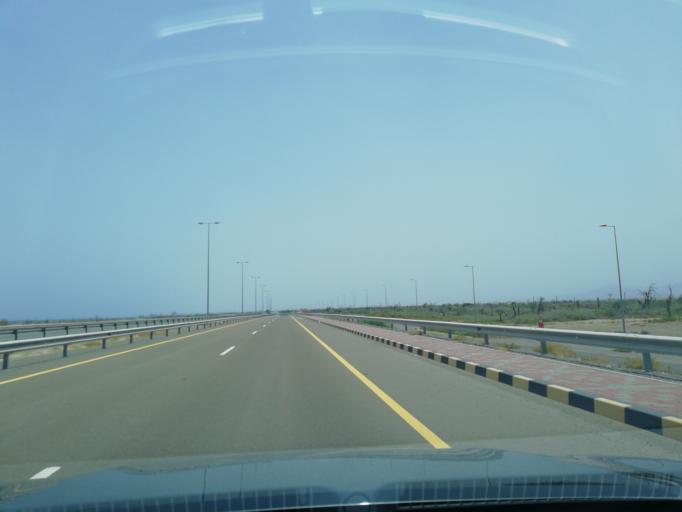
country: OM
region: Al Batinah
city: Shinas
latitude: 24.8805
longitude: 56.4041
